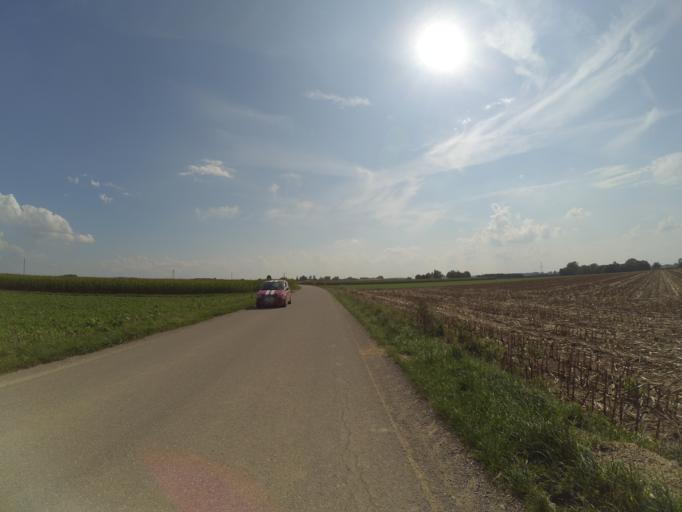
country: DE
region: Bavaria
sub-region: Swabia
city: Lamerdingen
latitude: 48.0954
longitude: 10.7698
